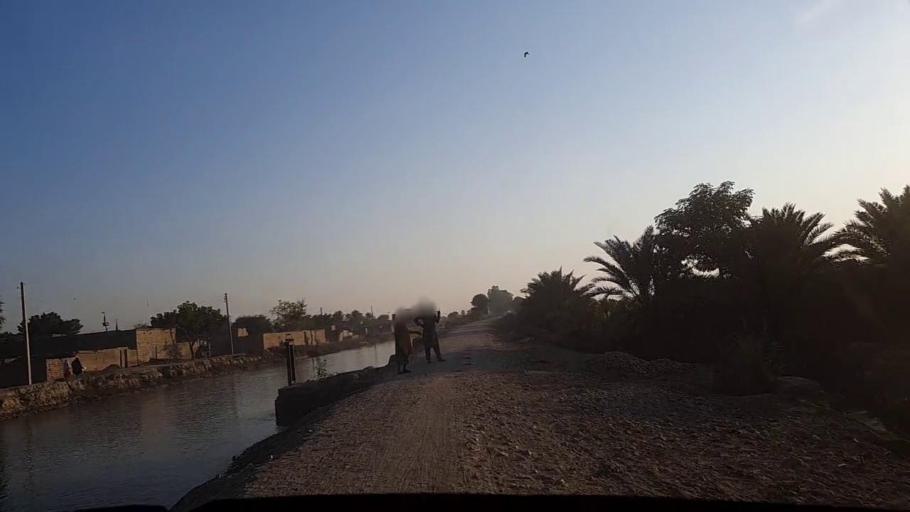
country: PK
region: Sindh
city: Sobhadero
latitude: 27.3877
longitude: 68.3829
